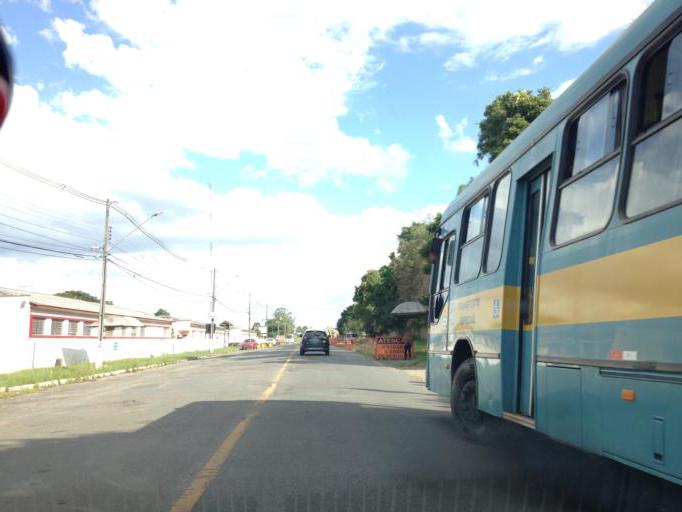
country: BR
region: Parana
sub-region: Pinhais
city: Pinhais
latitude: -25.4177
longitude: -49.2186
